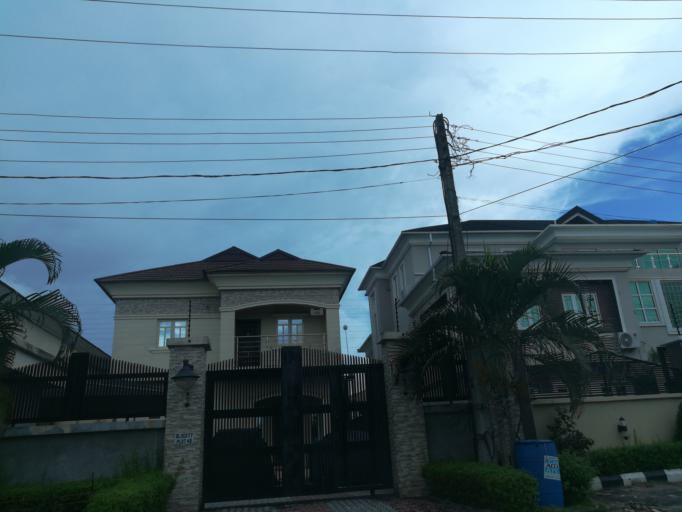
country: NG
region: Lagos
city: Ikoyi
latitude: 6.4469
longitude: 3.4783
